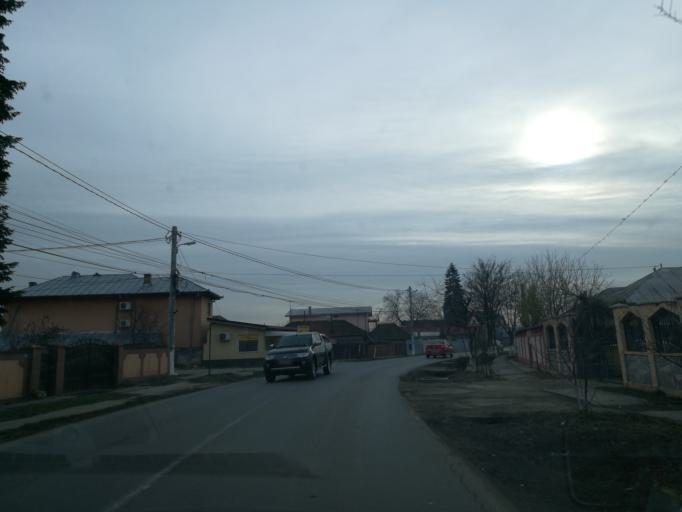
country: RO
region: Ilfov
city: Stefanestii de Jos
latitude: 44.5325
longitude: 26.2023
